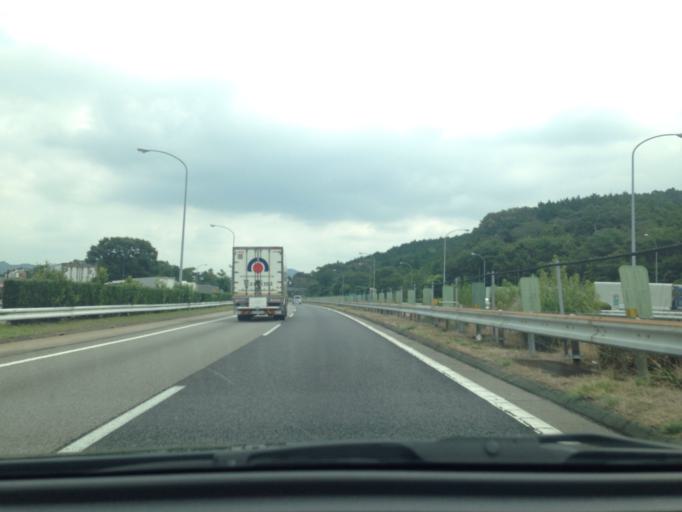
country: JP
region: Aichi
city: Shinshiro
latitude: 34.8432
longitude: 137.4974
